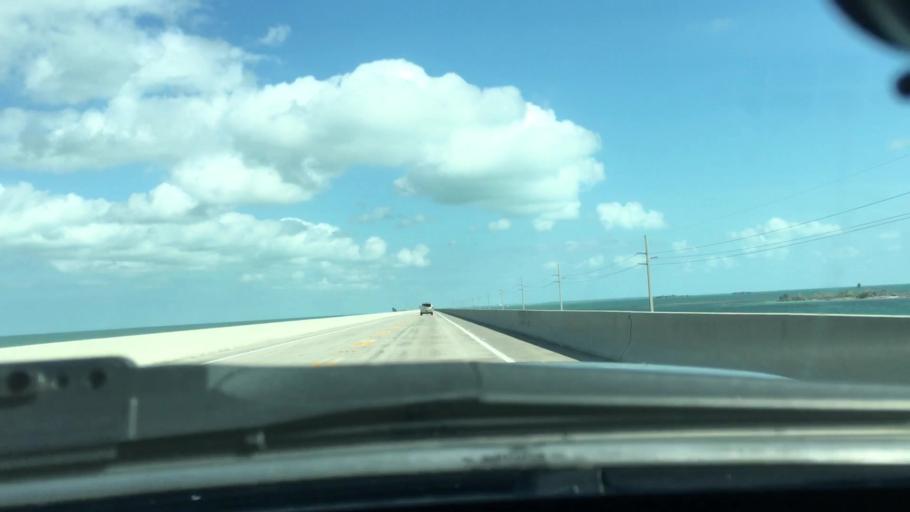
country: US
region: Florida
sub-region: Monroe County
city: Big Pine Key
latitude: 24.6842
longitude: -81.2214
